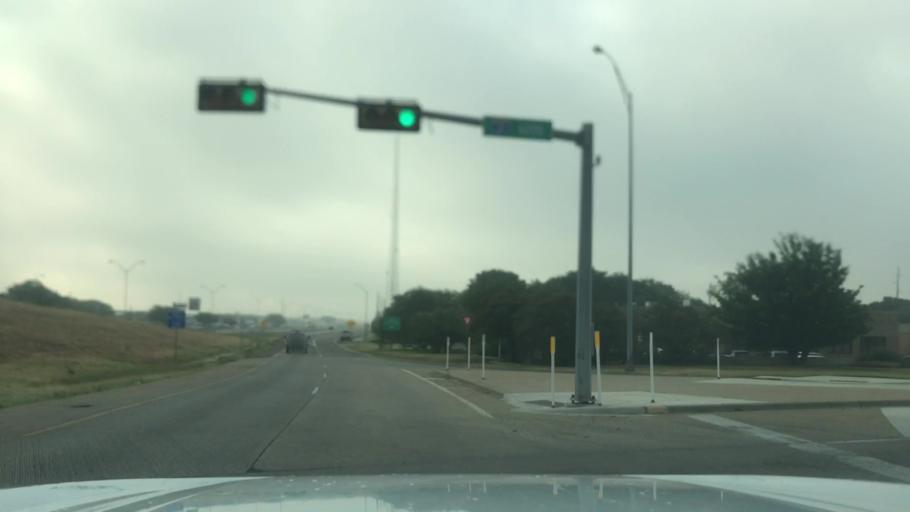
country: US
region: Texas
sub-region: Lubbock County
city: Lubbock
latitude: 33.5367
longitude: -101.8437
